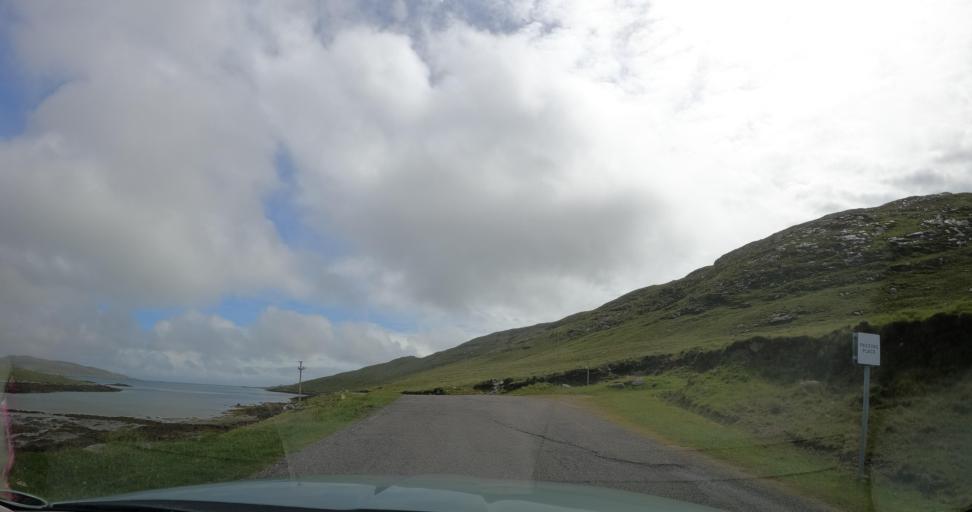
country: GB
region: Scotland
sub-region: Eilean Siar
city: Barra
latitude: 56.9393
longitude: -7.5415
